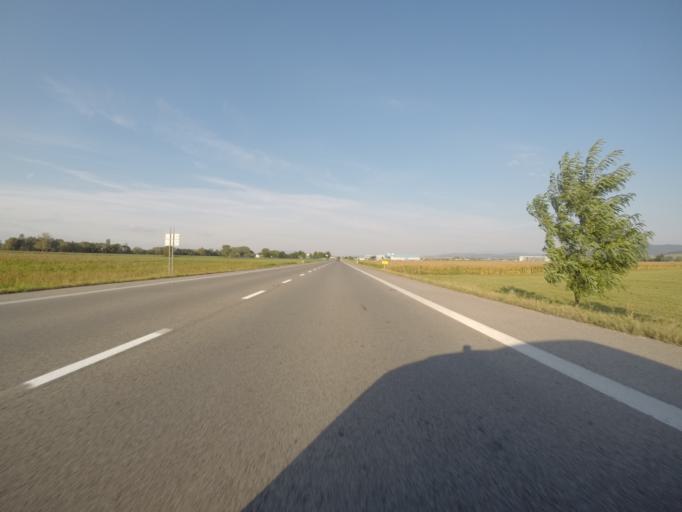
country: SK
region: Nitriansky
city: Banovce nad Bebravou
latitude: 48.5562
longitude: 18.1908
